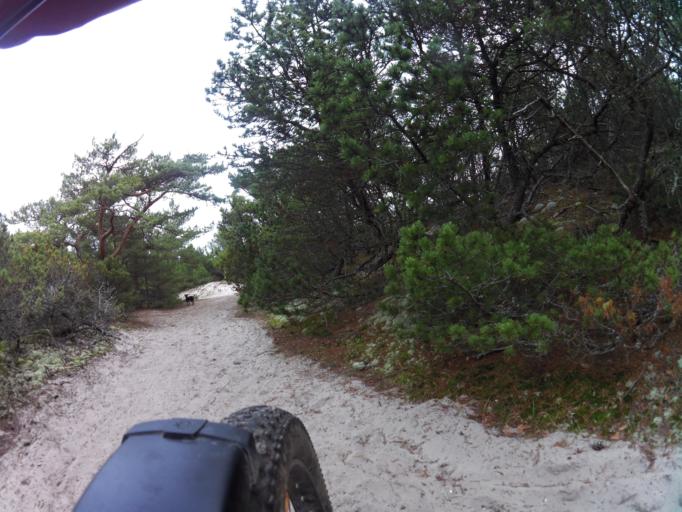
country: PL
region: Pomeranian Voivodeship
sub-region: Powiat pucki
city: Hel
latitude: 54.6277
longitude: 18.8172
